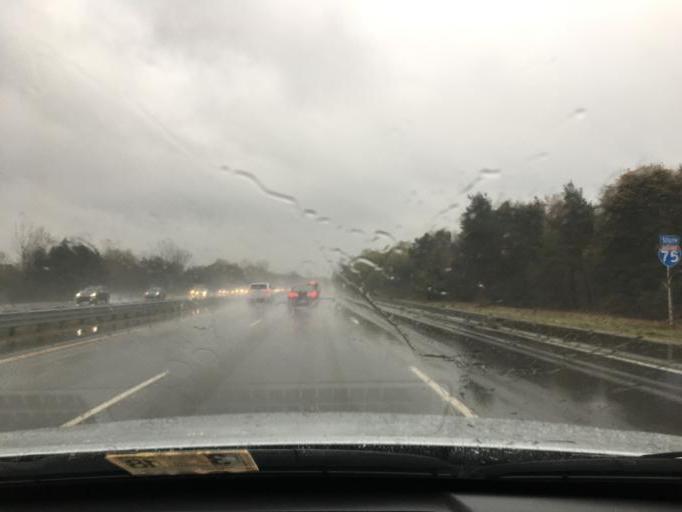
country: US
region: Michigan
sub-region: Oakland County
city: Clarkston
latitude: 42.7283
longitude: -83.3632
